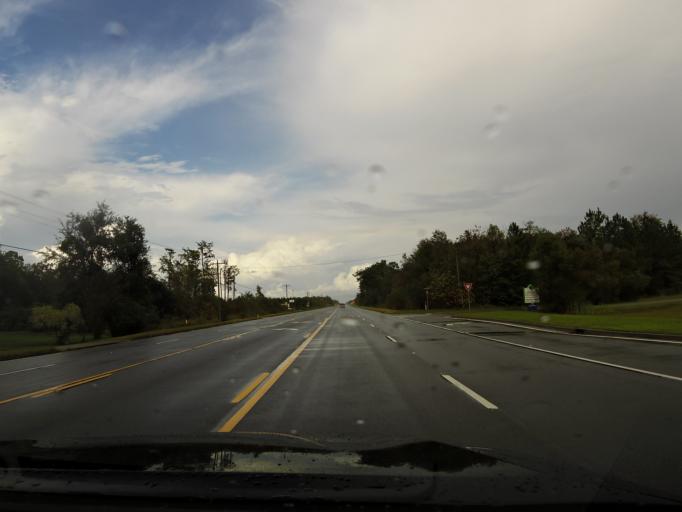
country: US
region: Georgia
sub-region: Long County
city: Ludowici
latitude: 31.7201
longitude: -81.7330
